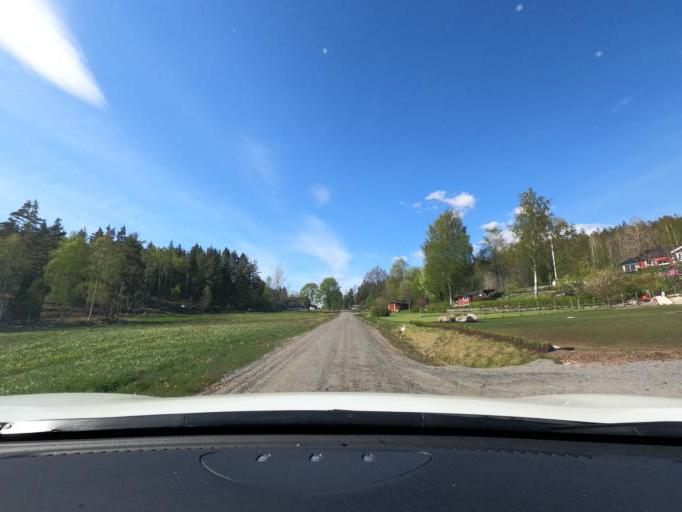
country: SE
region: Vaestra Goetaland
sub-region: Harryda Kommun
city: Ravlanda
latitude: 57.5896
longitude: 12.4884
